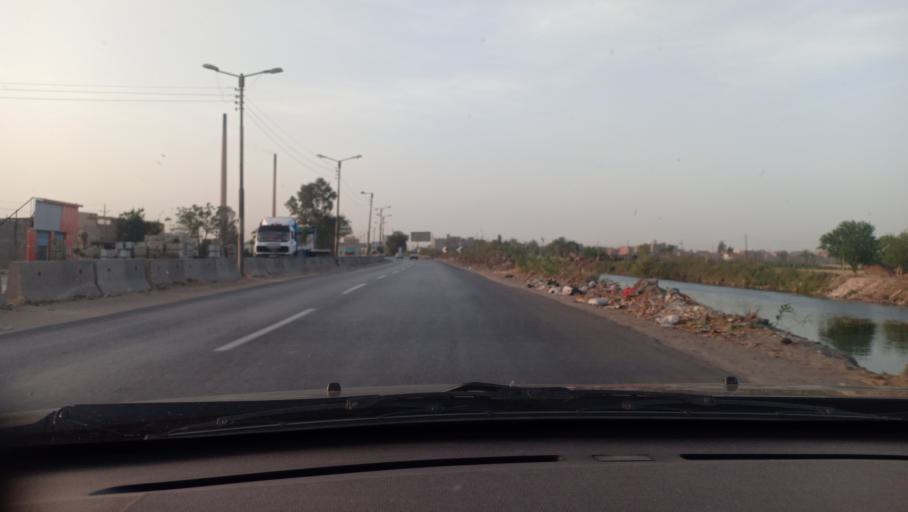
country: EG
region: Muhafazat al Gharbiyah
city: Zifta
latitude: 30.6271
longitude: 31.2795
